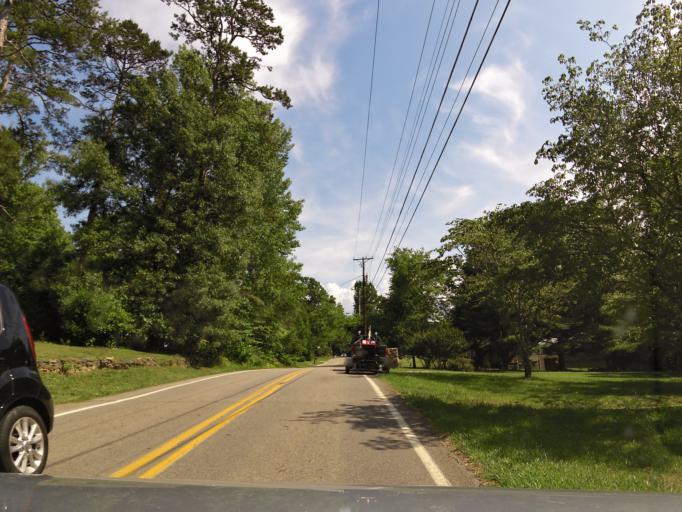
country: US
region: Tennessee
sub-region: Knox County
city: Knoxville
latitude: 35.9554
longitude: -83.8887
